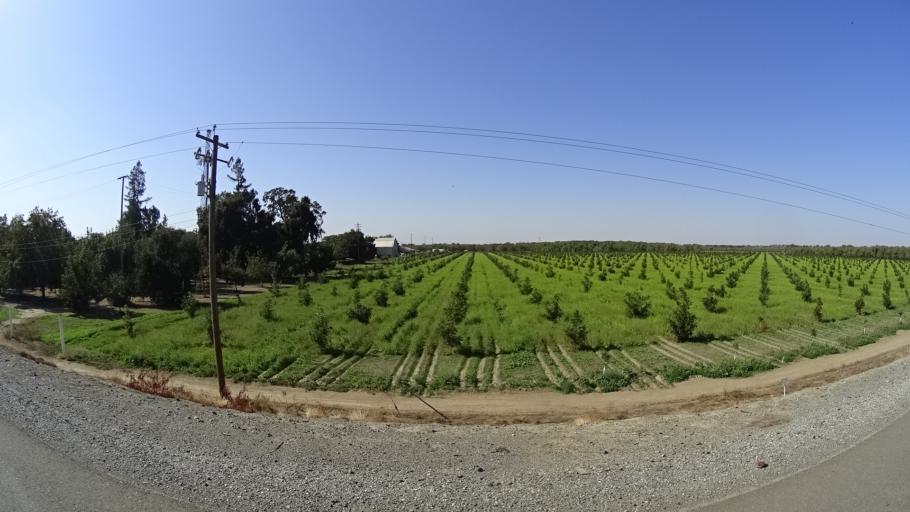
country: US
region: California
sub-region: Yolo County
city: West Sacramento
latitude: 38.6260
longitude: -121.5637
